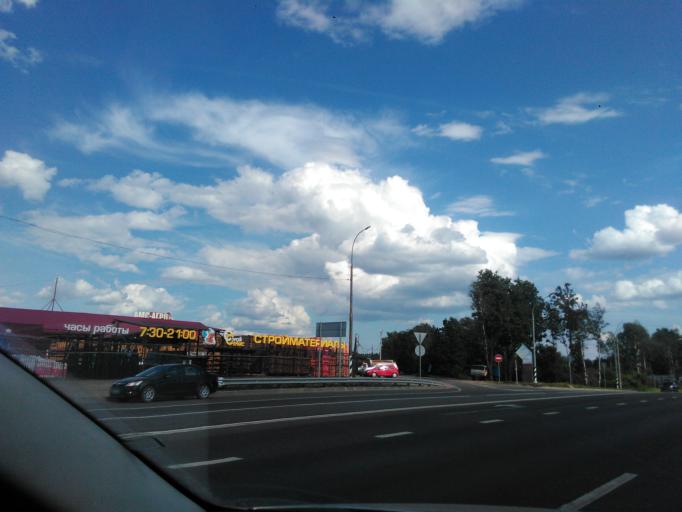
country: RU
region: Moskovskaya
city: Peshki
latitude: 56.1543
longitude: 37.0303
